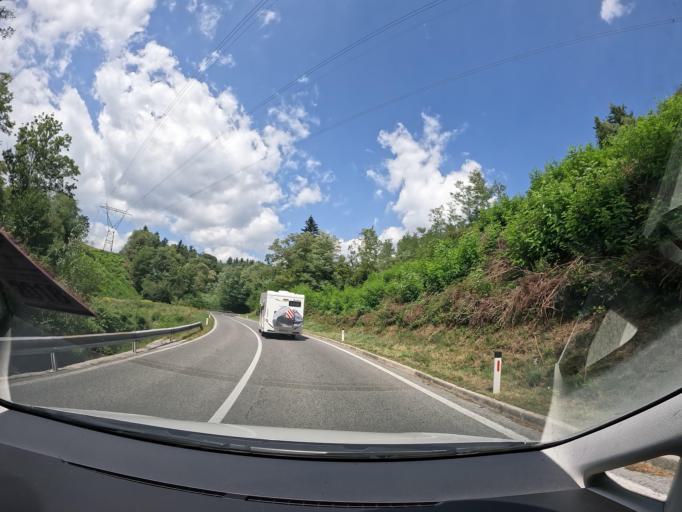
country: SI
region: Ilirska Bistrica
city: Ilirska Bistrica
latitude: 45.5328
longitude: 14.2522
